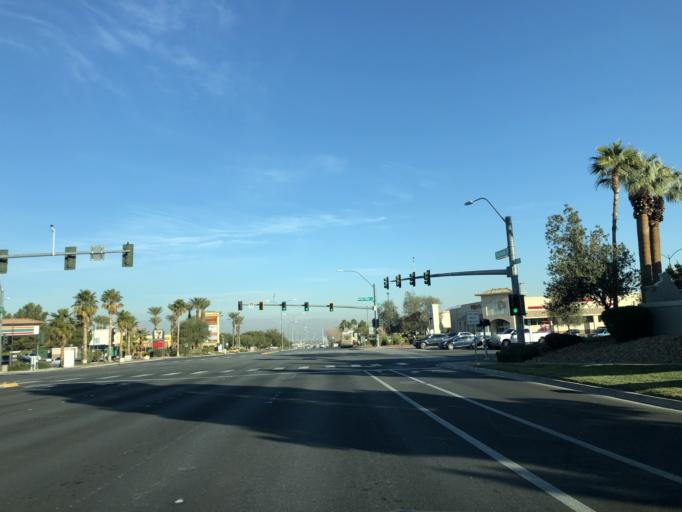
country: US
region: Nevada
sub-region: Clark County
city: Whitney
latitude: 36.0211
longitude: -115.0472
